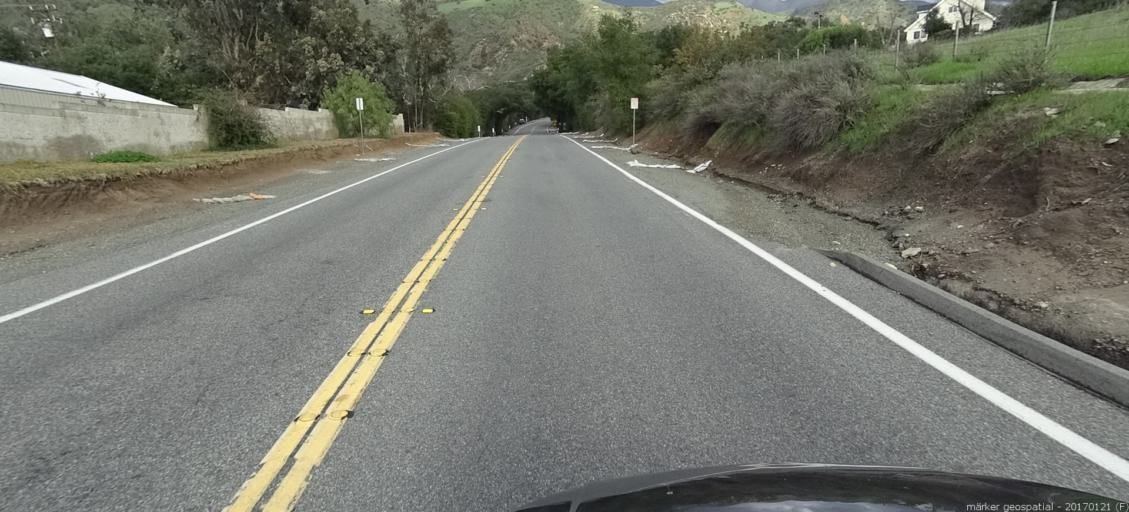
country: US
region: California
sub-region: Orange County
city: Portola Hills
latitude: 33.6850
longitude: -117.6177
